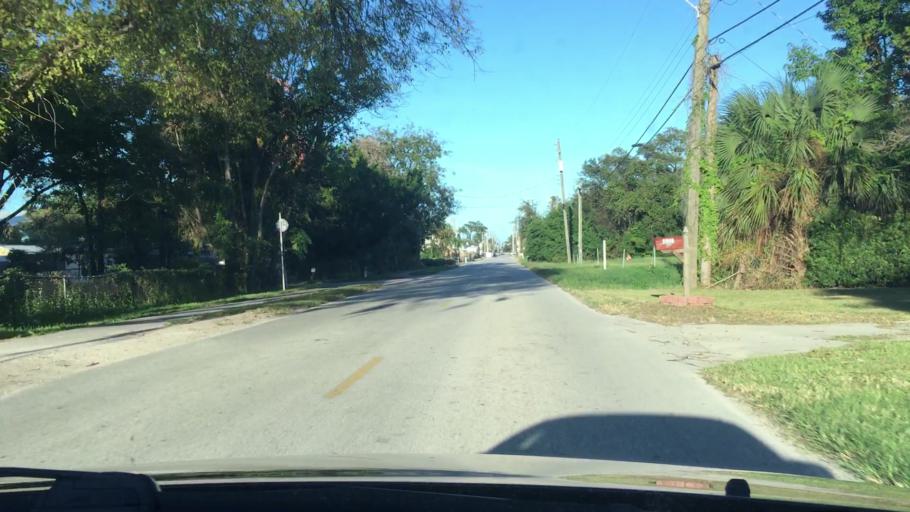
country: US
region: Florida
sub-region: Volusia County
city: Holly Hill
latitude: 29.2292
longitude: -81.0392
